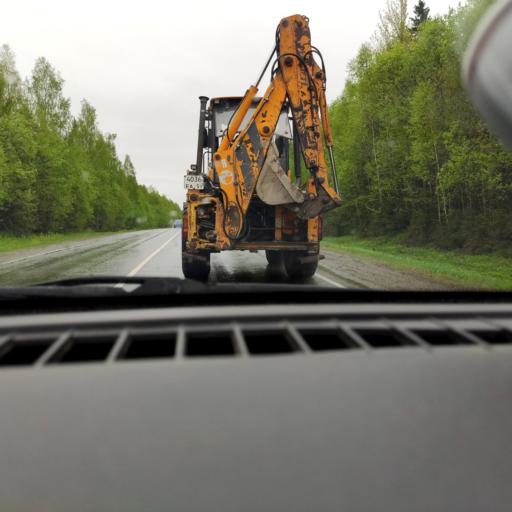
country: RU
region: Perm
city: Perm
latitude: 58.1795
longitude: 56.2262
